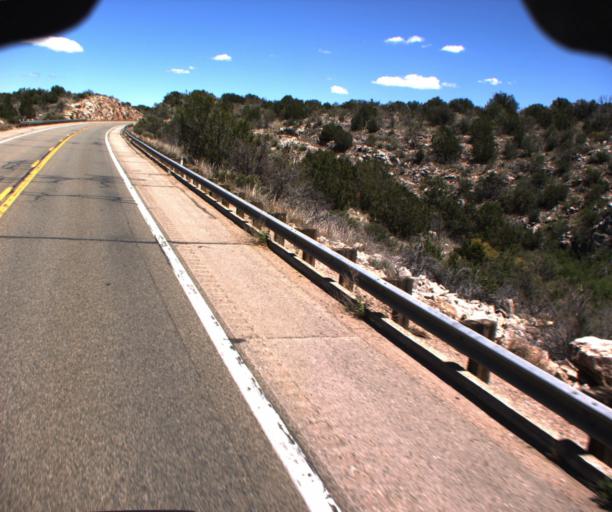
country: US
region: Arizona
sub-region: Yavapai County
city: Paulden
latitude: 34.9297
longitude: -112.4431
